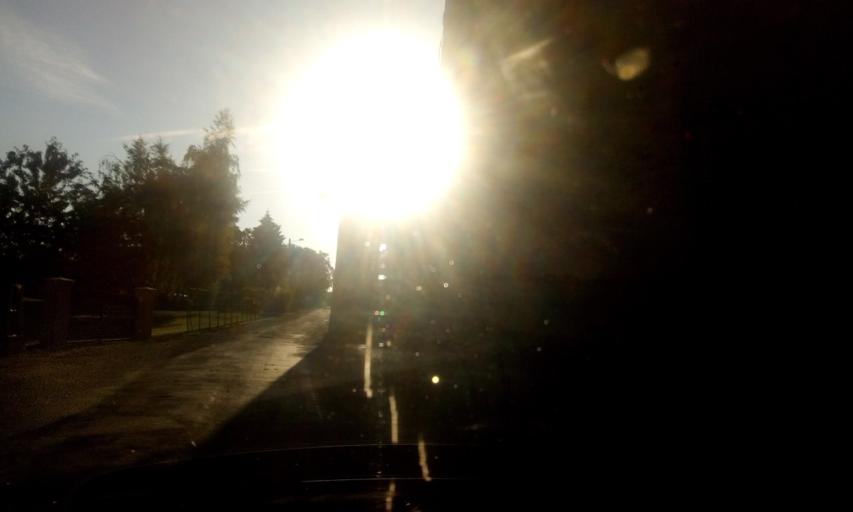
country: FR
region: Rhone-Alpes
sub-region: Departement de l'Isere
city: Izeaux
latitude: 45.3319
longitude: 5.4287
